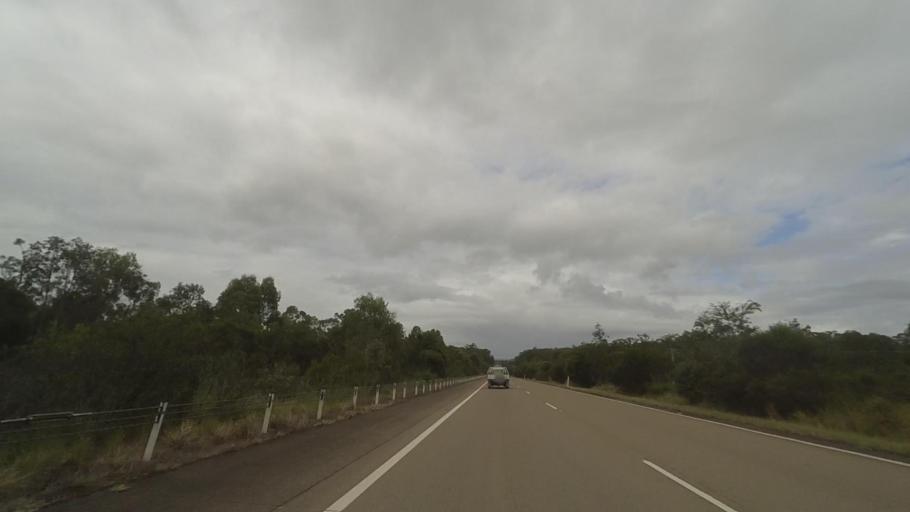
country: AU
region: New South Wales
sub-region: Port Stephens Shire
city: Medowie
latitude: -32.6366
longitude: 151.9343
